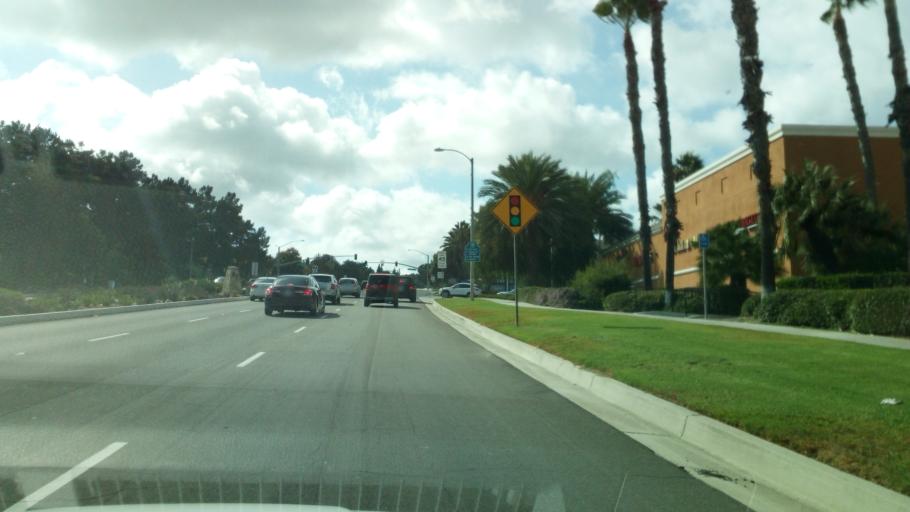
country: US
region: California
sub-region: Orange County
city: Aliso Viejo
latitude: 33.5708
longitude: -117.7245
